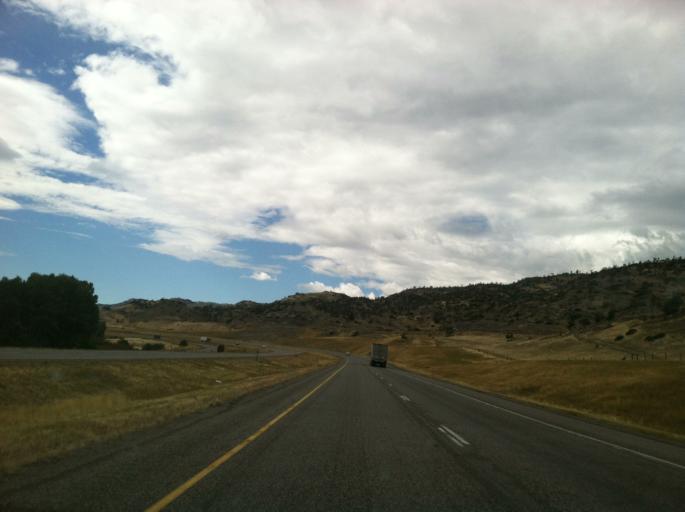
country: US
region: Montana
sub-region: Park County
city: Livingston
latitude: 45.6605
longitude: -110.6373
